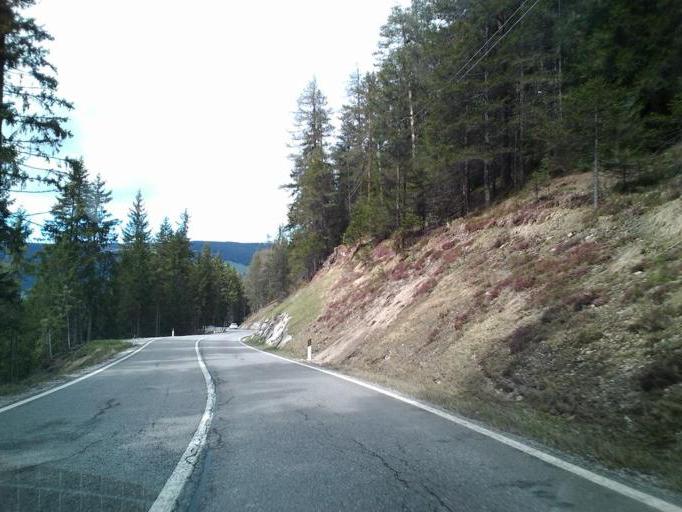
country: IT
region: Trentino-Alto Adige
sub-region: Bolzano
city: Dobbiaco
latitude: 46.7105
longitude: 12.2240
